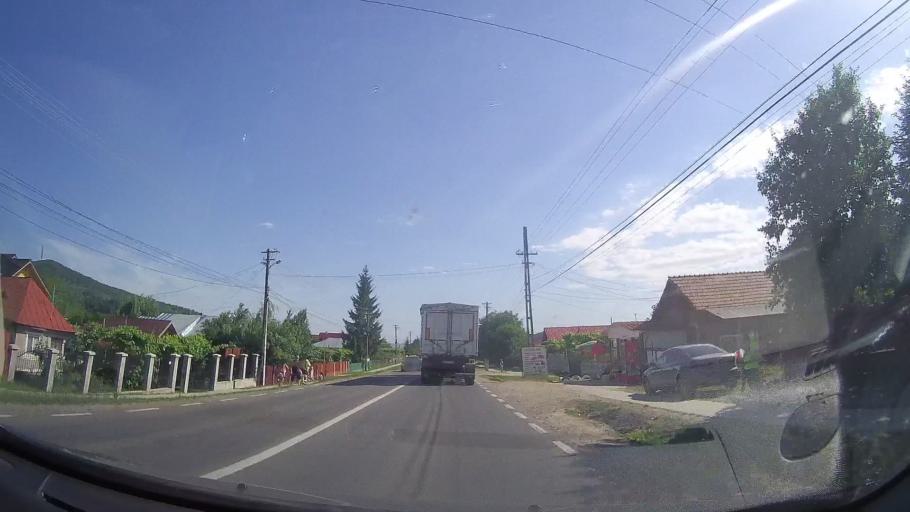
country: RO
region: Prahova
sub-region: Comuna Gura Vitioarei
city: Gura Vitioarei
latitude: 45.1598
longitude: 26.0303
